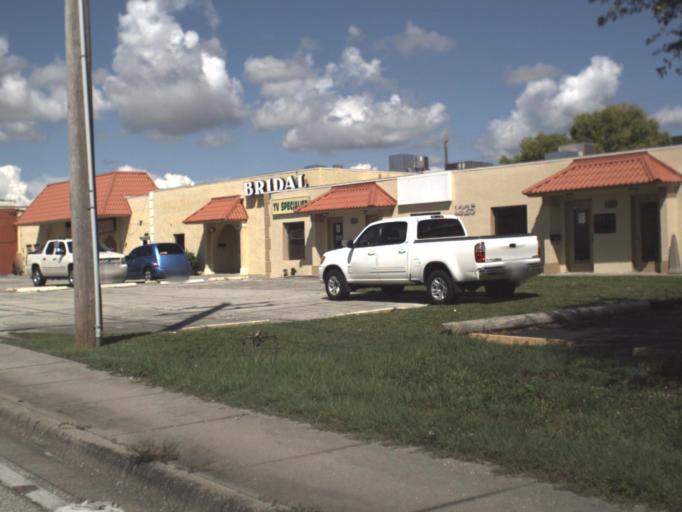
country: US
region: Florida
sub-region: Lee County
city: Lochmoor Waterway Estates
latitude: 26.6272
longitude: -81.9407
